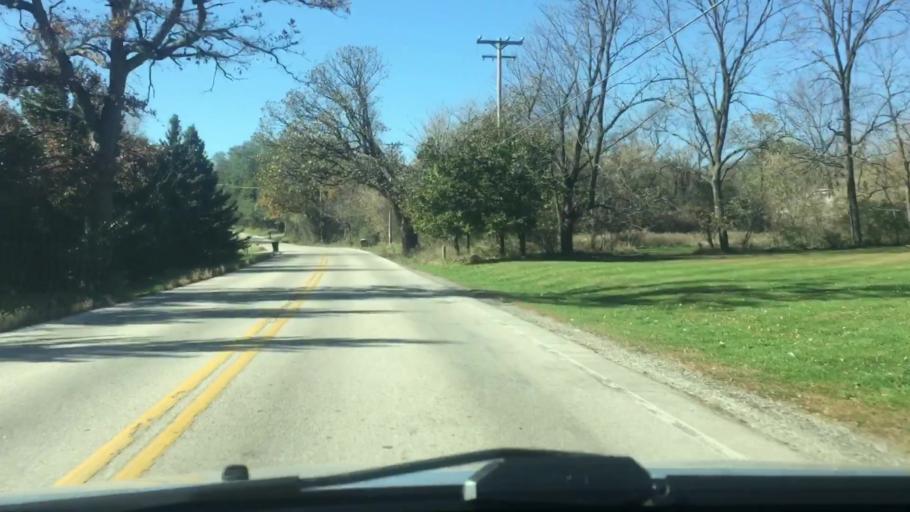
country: US
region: Wisconsin
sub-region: Waukesha County
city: Wales
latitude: 42.9921
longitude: -88.3708
